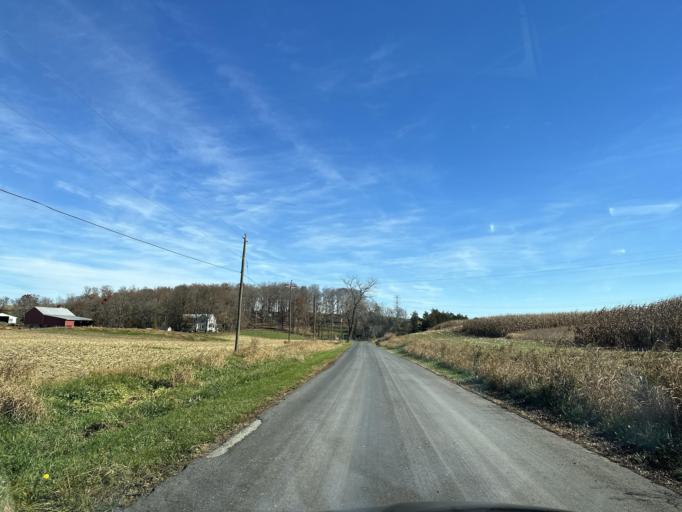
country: US
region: Virginia
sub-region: Rockingham County
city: Bridgewater
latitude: 38.3300
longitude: -78.9619
